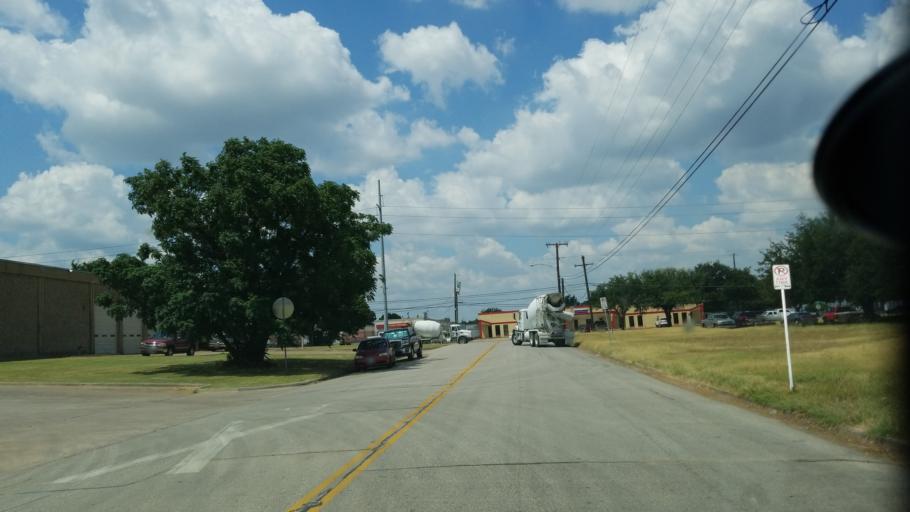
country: US
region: Texas
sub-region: Dallas County
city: Duncanville
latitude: 32.6851
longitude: -96.8904
